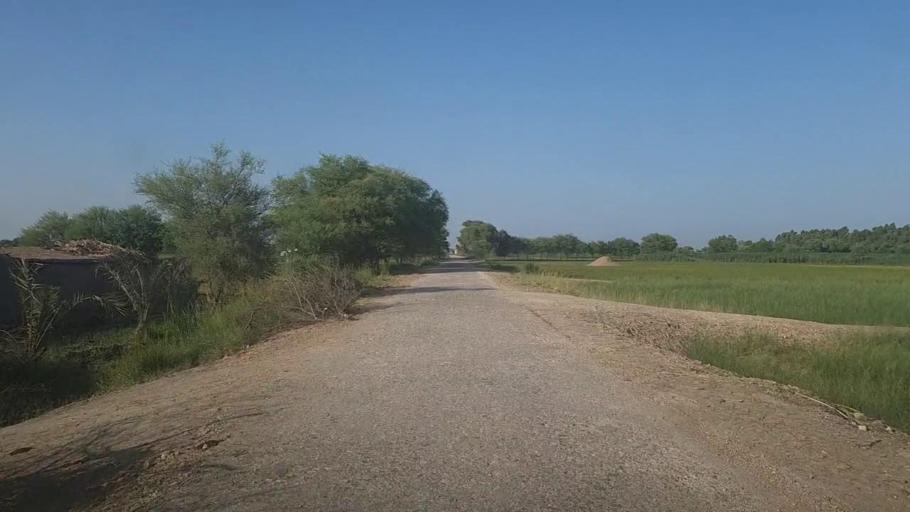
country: PK
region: Sindh
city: Khairpur
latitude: 28.1041
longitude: 69.6322
